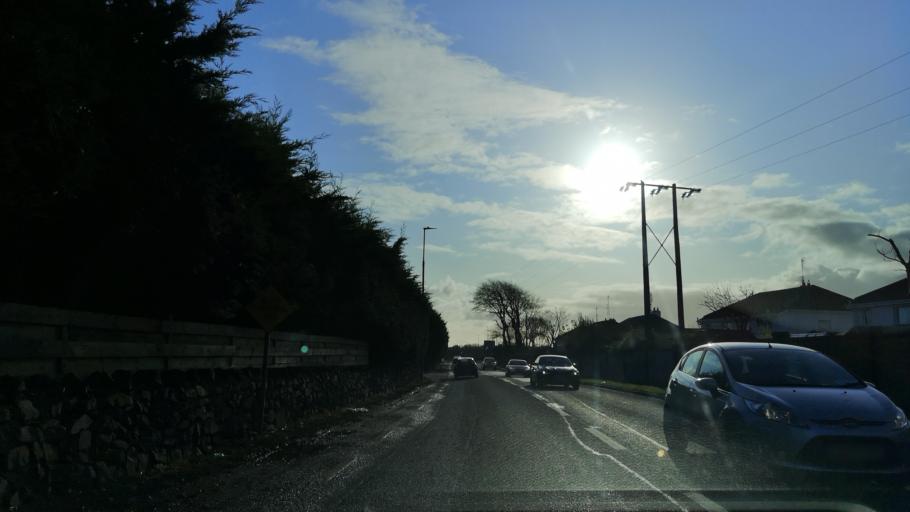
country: IE
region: Connaught
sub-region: County Galway
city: Oranmore
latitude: 53.2762
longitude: -8.9271
